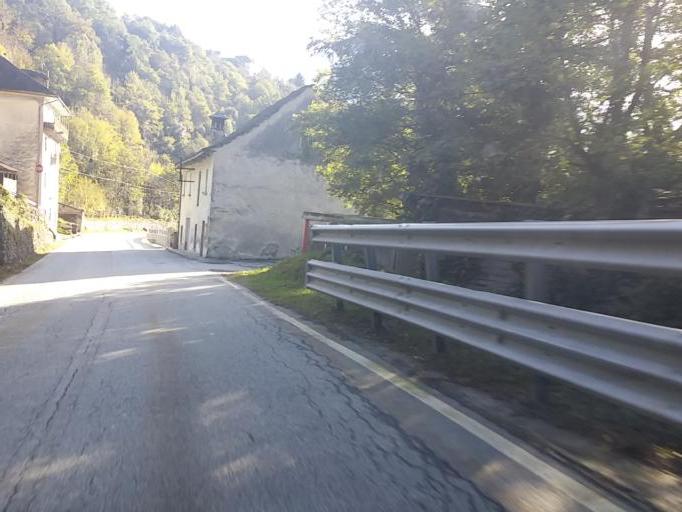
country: IT
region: Piedmont
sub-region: Provincia Verbano-Cusio-Ossola
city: Crevoladossola
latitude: 46.1548
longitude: 8.2932
